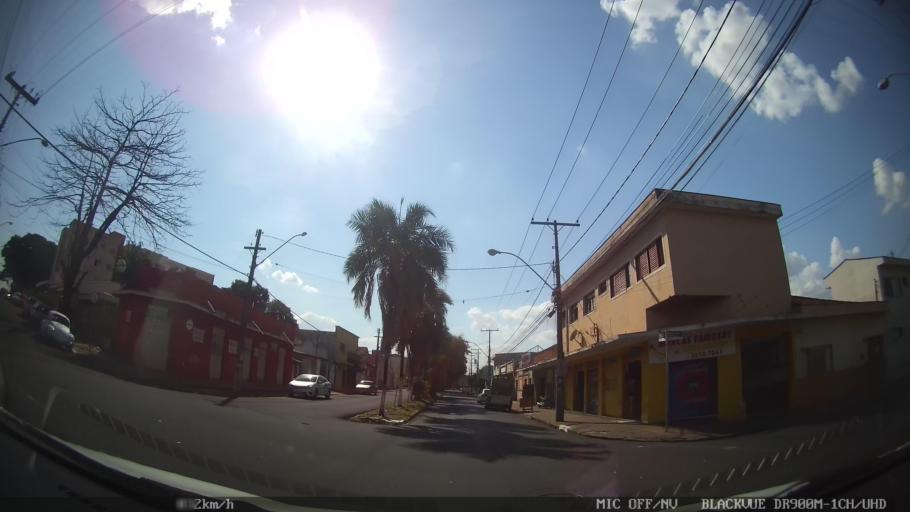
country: BR
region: Sao Paulo
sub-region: Ribeirao Preto
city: Ribeirao Preto
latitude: -21.1815
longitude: -47.8225
